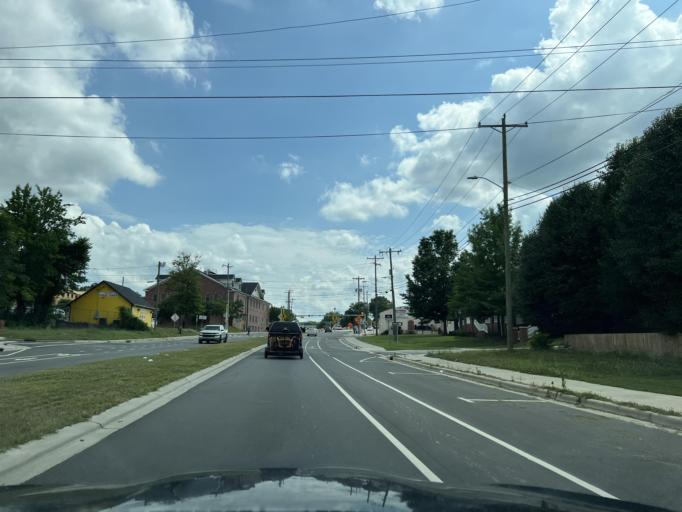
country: US
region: North Carolina
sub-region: Durham County
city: Durham
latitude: 35.9893
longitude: -78.8868
